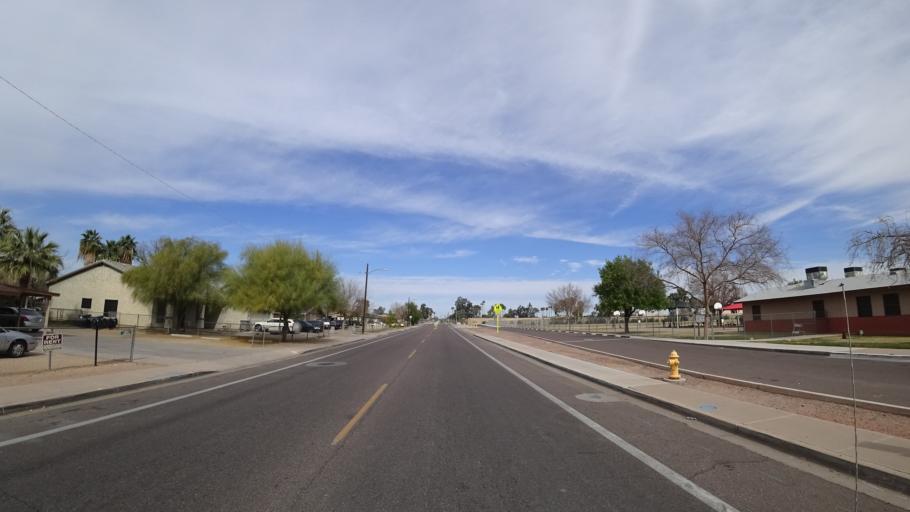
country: US
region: Arizona
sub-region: Maricopa County
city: Phoenix
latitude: 33.4598
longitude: -112.1259
